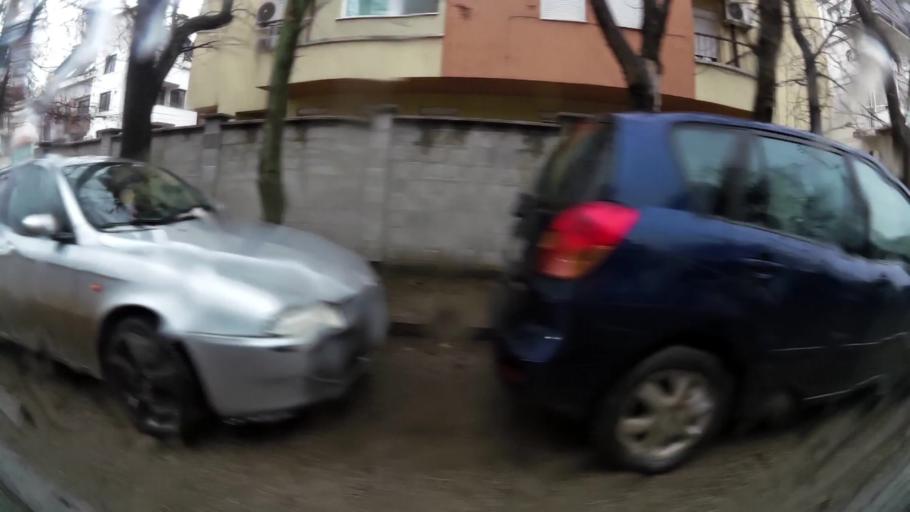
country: BG
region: Sofia-Capital
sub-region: Stolichna Obshtina
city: Sofia
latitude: 42.6501
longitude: 23.3321
